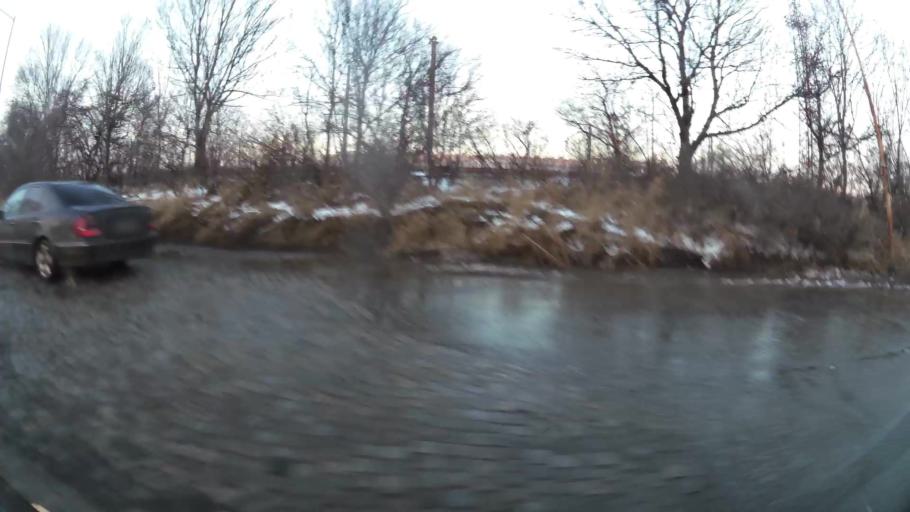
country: BG
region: Sofia-Capital
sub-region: Stolichna Obshtina
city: Sofia
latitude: 42.6925
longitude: 23.3688
